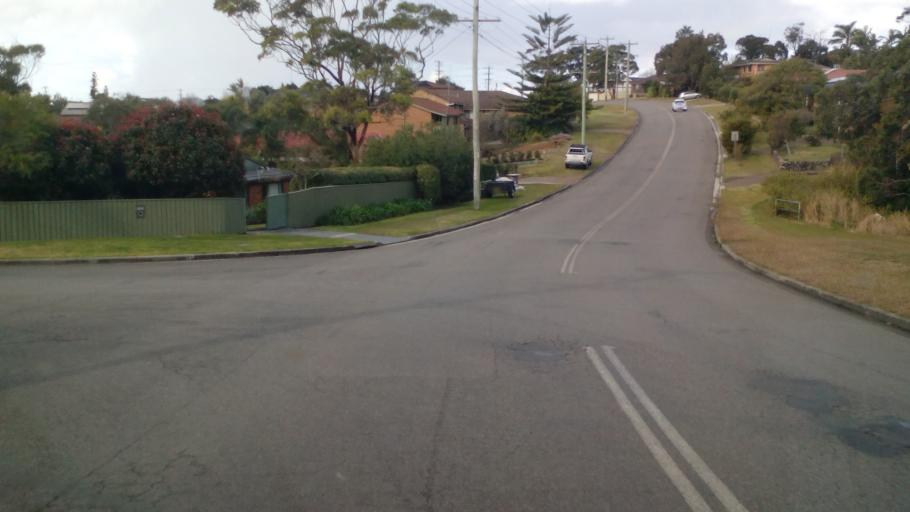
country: AU
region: New South Wales
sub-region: Lake Macquarie Shire
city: Kahibah
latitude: -32.9809
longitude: 151.7144
